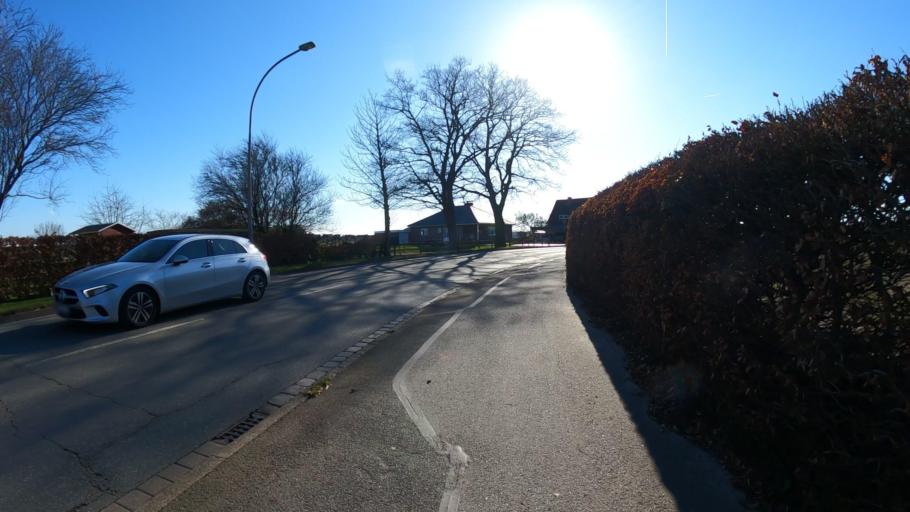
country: DE
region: Schleswig-Holstein
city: Rellingen
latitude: 53.6382
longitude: 9.8052
